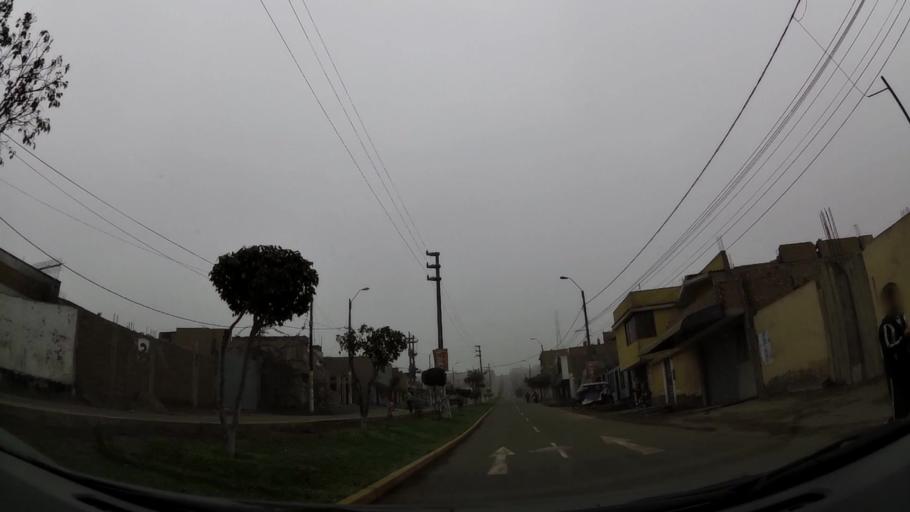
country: PE
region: Lima
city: Ventanilla
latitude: -11.8347
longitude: -77.1086
